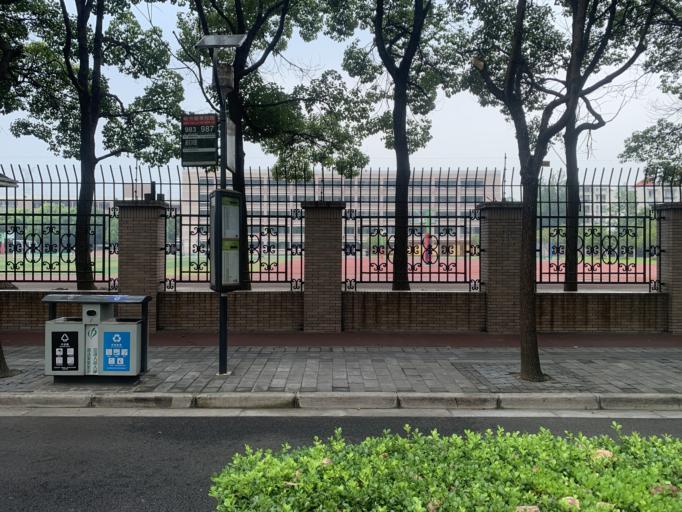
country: CN
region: Shanghai Shi
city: Huamu
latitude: 31.2345
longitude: 121.5705
